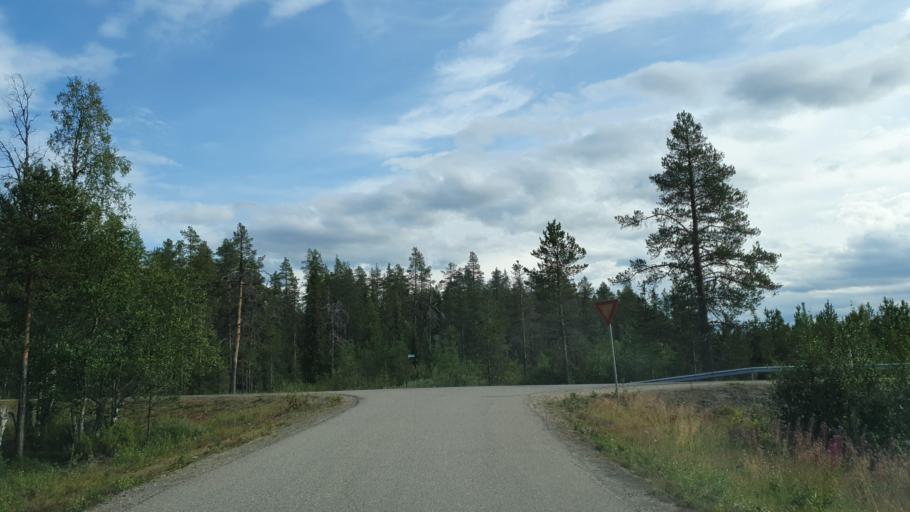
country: FI
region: Lapland
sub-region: Tunturi-Lappi
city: Muonio
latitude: 67.7065
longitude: 24.1272
